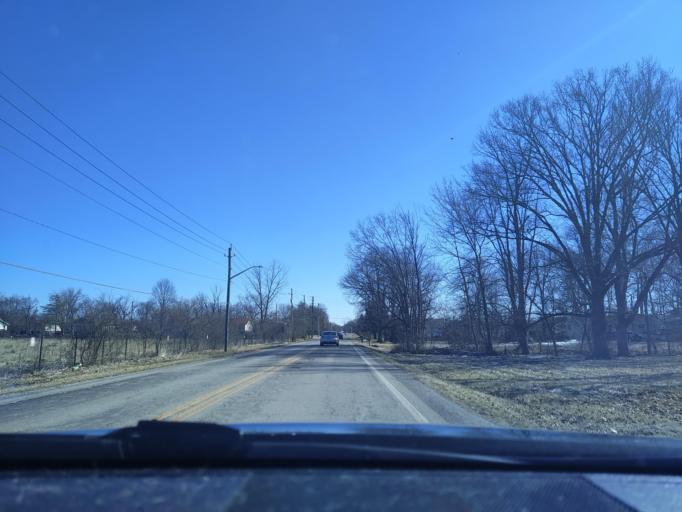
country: US
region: Indiana
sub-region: Marion County
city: Meridian Hills
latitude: 39.8973
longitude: -86.2003
